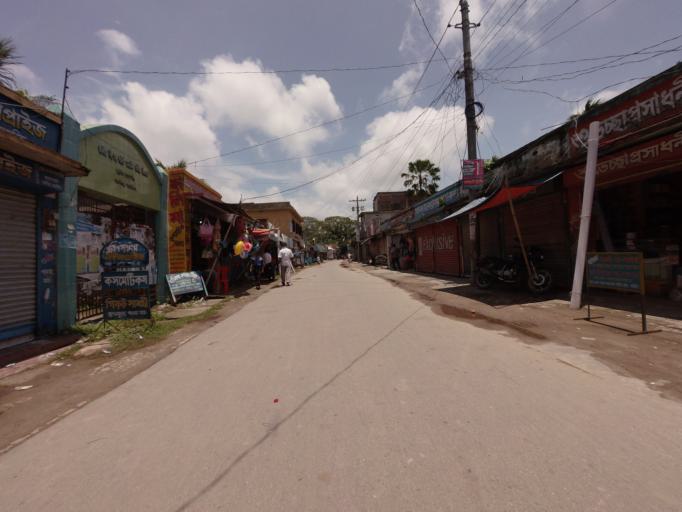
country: BD
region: Khulna
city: Kalia
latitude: 23.0398
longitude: 89.6318
